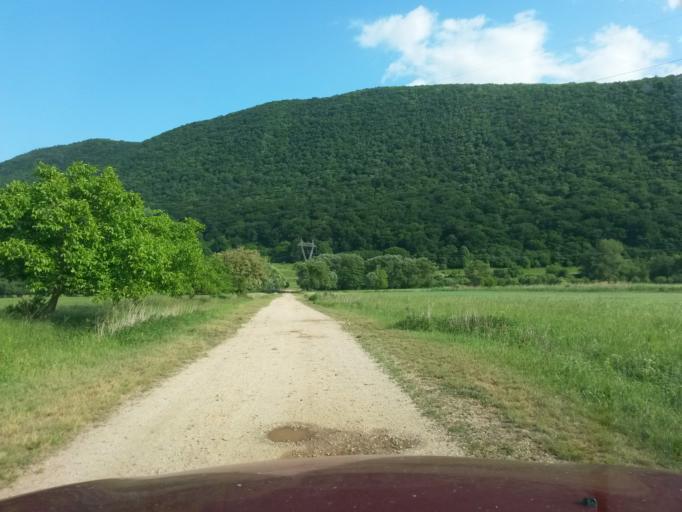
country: SK
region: Kosicky
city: Roznava
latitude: 48.5856
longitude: 20.6759
